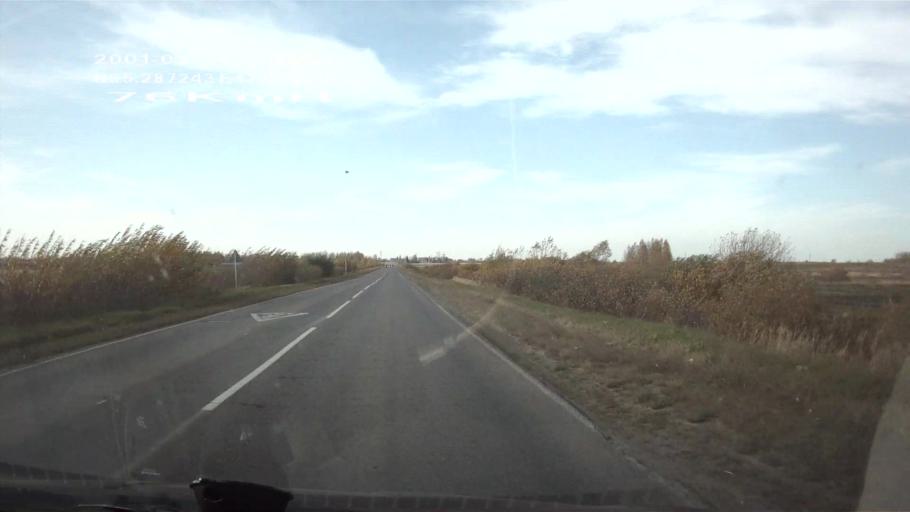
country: RU
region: Chuvashia
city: Ibresi
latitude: 55.2873
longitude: 47.0755
